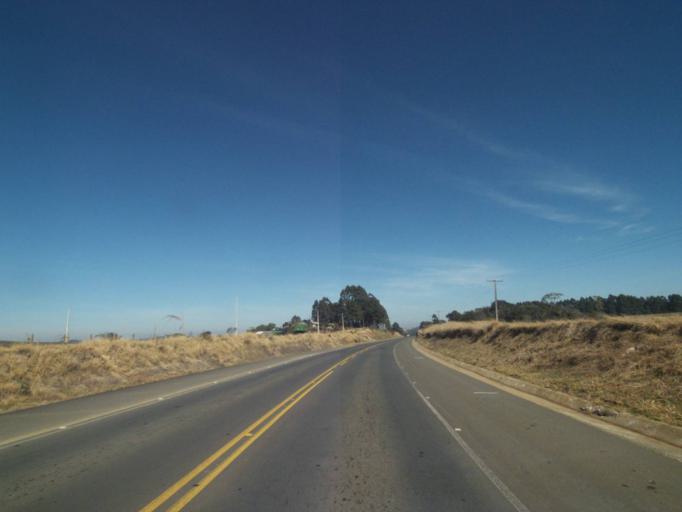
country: BR
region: Parana
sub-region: Tibagi
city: Tibagi
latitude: -24.8013
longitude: -50.4682
